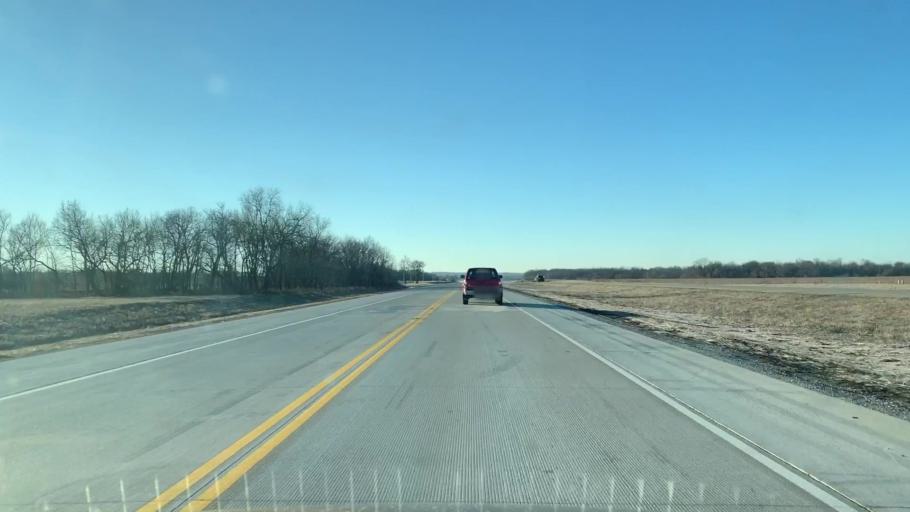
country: US
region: Kansas
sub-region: Bourbon County
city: Fort Scott
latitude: 37.7216
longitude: -94.7042
